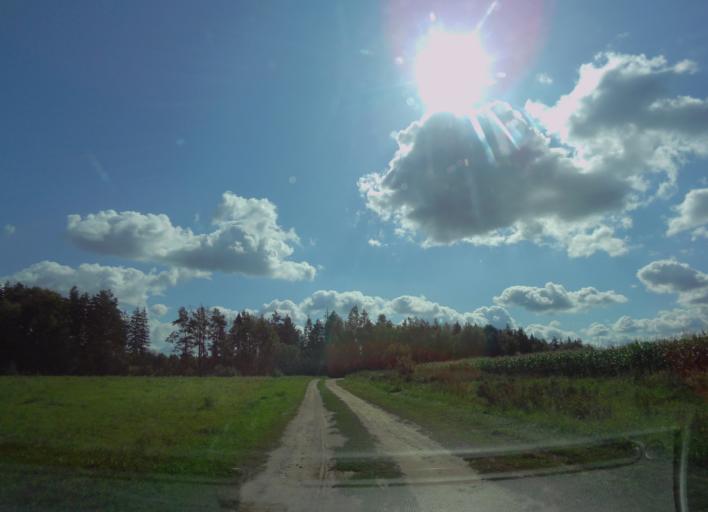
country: BY
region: Minsk
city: Zyembin
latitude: 54.3852
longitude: 28.3880
